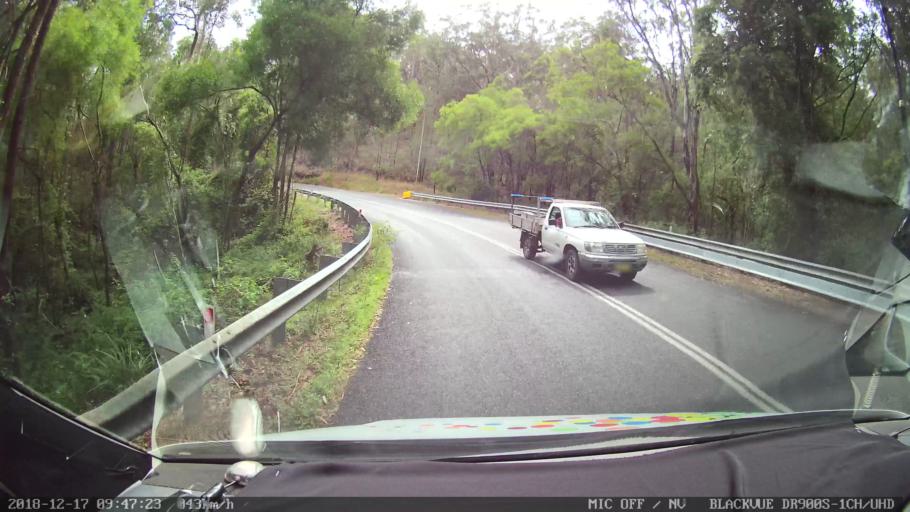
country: AU
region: New South Wales
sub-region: Tenterfield Municipality
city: Carrolls Creek
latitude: -28.9288
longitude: 152.3376
